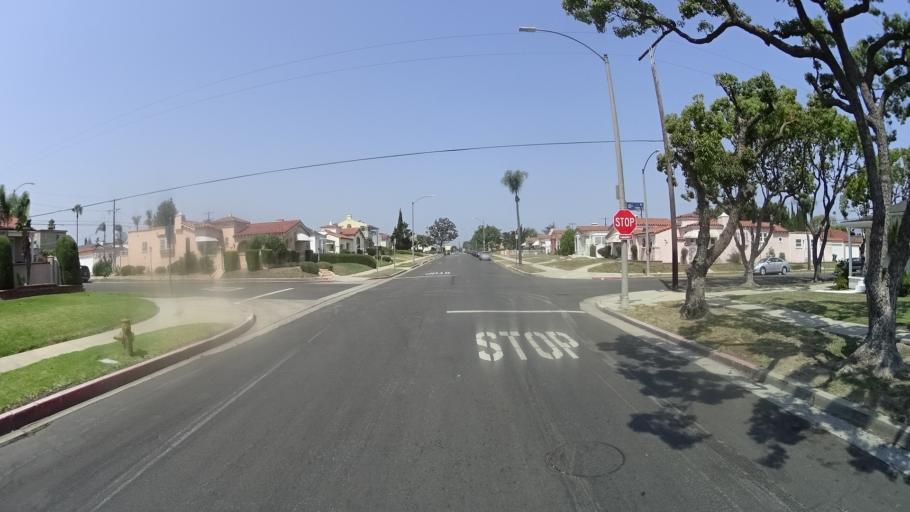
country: US
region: California
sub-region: Los Angeles County
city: Inglewood
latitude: 33.9691
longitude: -118.3284
